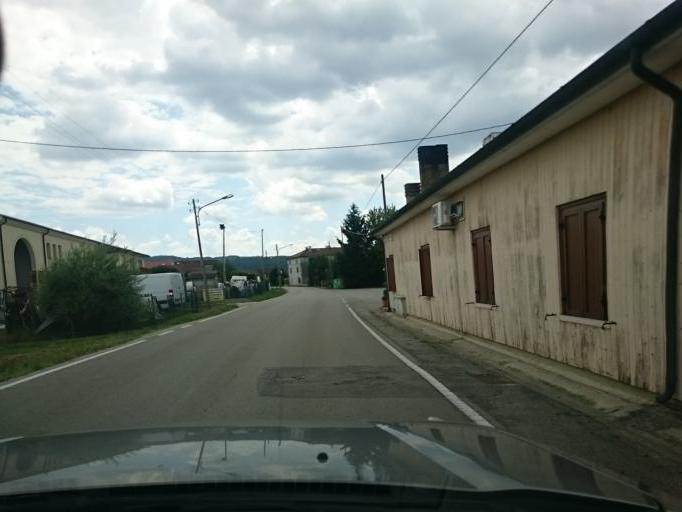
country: IT
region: Veneto
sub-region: Provincia di Vicenza
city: Torri di Quartesolo
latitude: 45.5139
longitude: 11.5844
